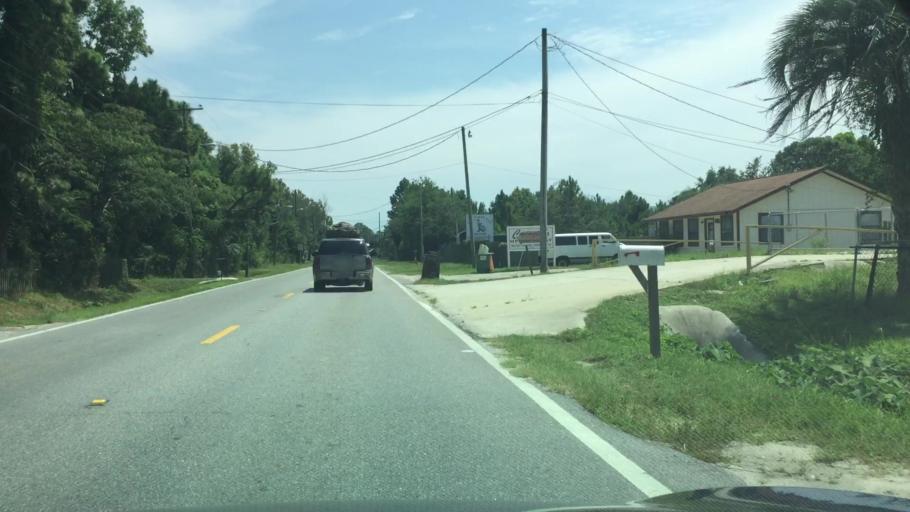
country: US
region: Florida
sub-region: Bay County
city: Panama City Beach
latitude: 30.1833
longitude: -85.7927
